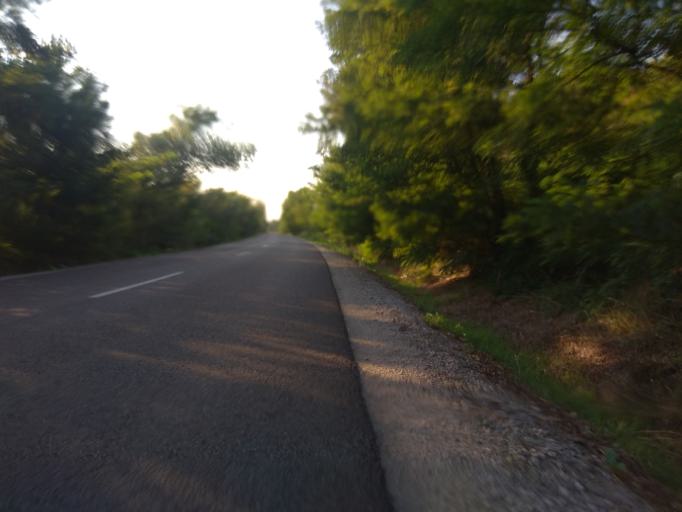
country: HU
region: Borsod-Abauj-Zemplen
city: Nyekladhaza
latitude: 47.9652
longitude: 20.8589
